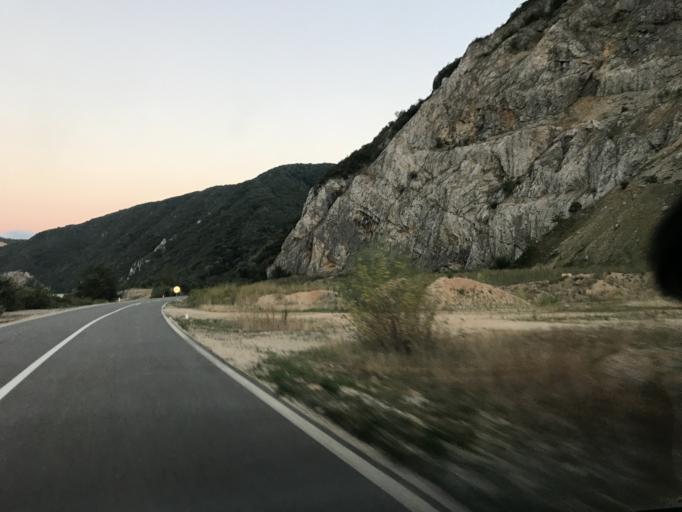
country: RO
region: Caras-Severin
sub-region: Comuna Pescari
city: Coronini
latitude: 44.6601
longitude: 21.6999
